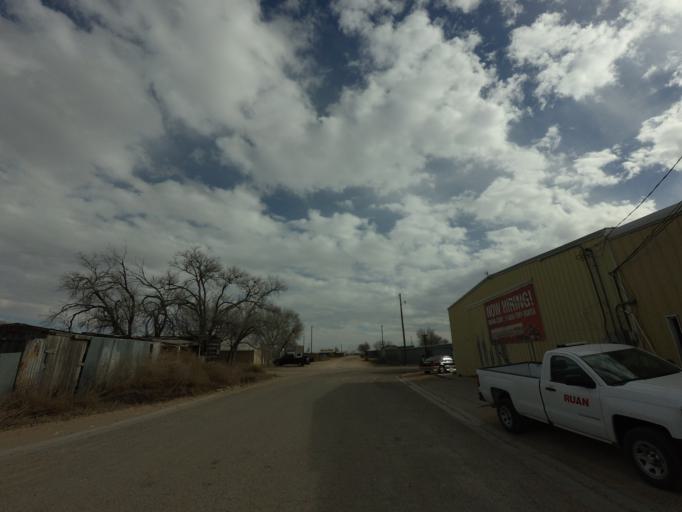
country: US
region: New Mexico
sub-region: Curry County
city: Clovis
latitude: 34.3928
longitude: -103.2171
